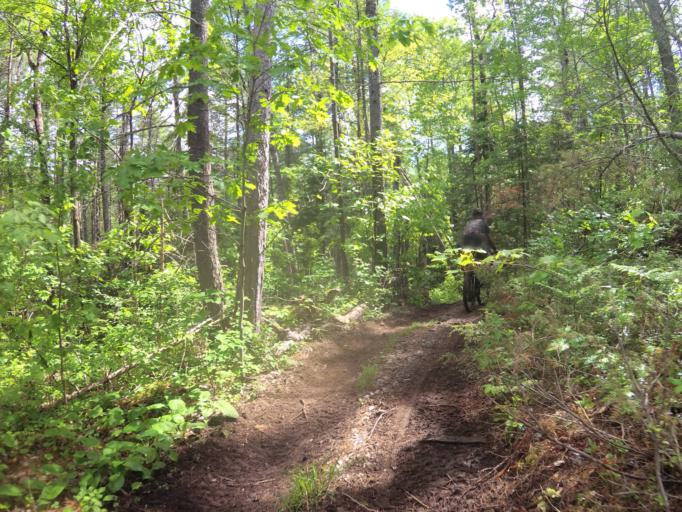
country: CA
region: Ontario
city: Renfrew
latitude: 45.1257
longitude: -76.8426
